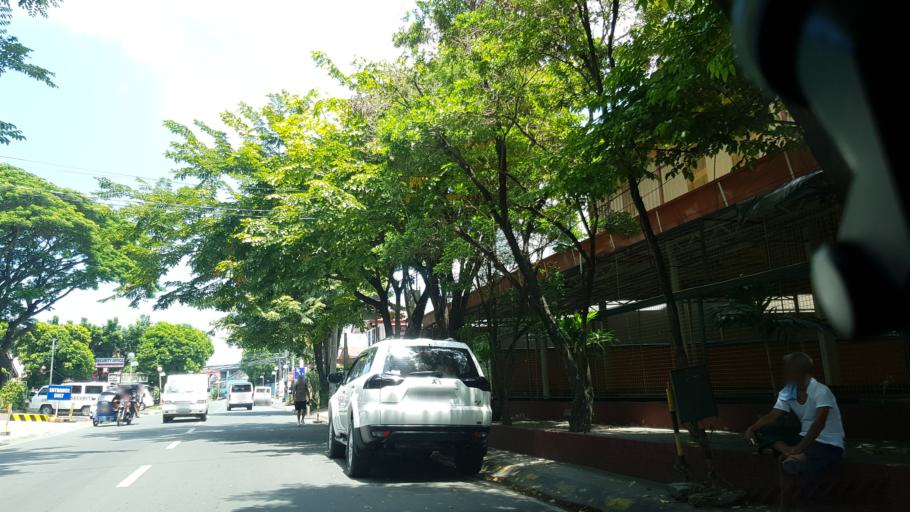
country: PH
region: Calabarzon
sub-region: Province of Rizal
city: Las Pinas
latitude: 14.4389
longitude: 120.9847
